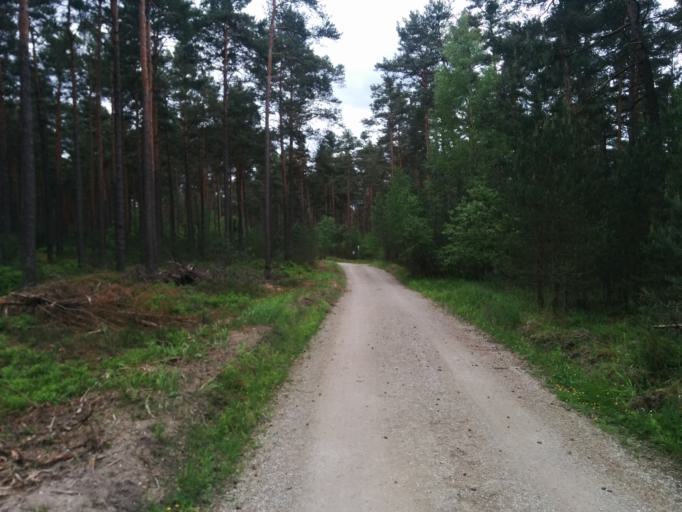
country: DE
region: Bavaria
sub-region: Regierungsbezirk Mittelfranken
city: Uttenreuth
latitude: 49.5449
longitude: 11.0761
